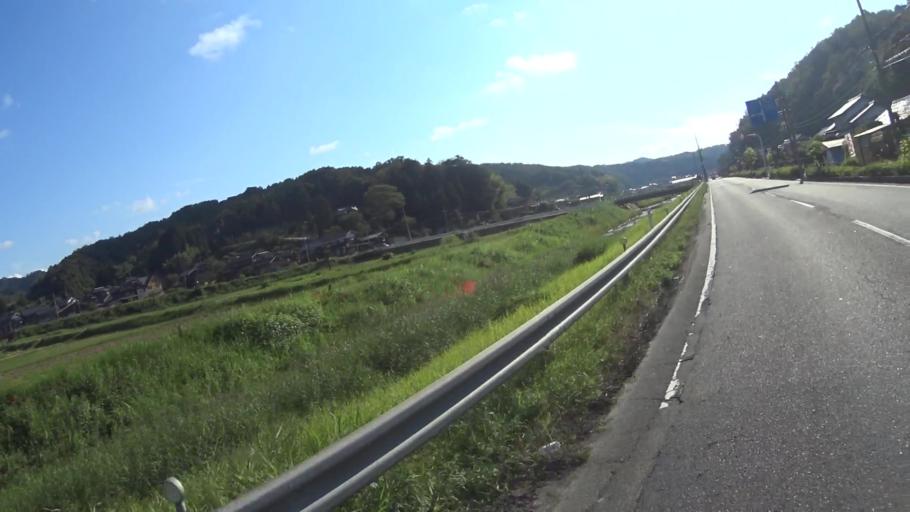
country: JP
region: Hyogo
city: Toyooka
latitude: 35.6557
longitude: 134.9854
